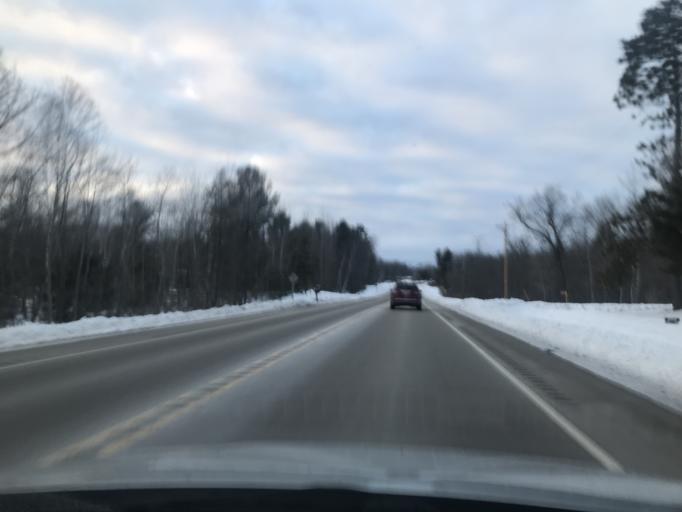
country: US
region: Wisconsin
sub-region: Marinette County
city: Marinette
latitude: 45.1593
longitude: -87.7193
